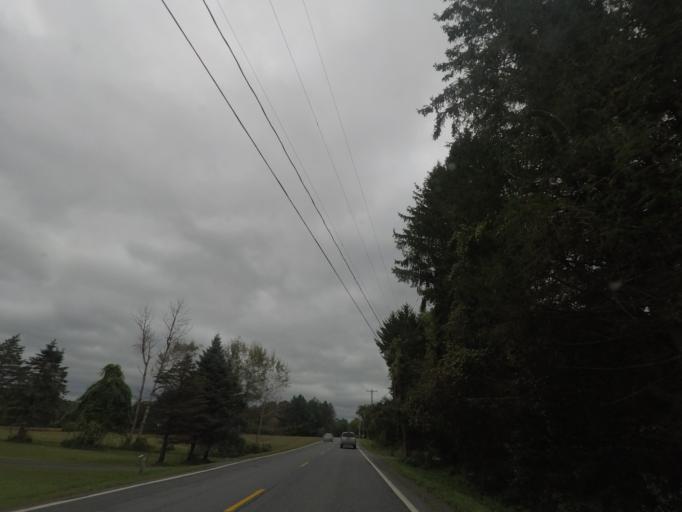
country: US
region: New York
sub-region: Rensselaer County
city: Hoosick Falls
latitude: 42.9523
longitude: -73.4190
